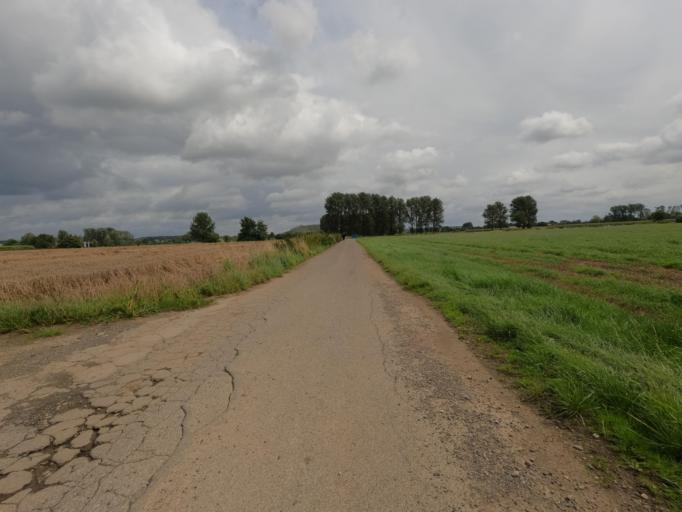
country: DE
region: North Rhine-Westphalia
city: Huckelhoven
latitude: 51.0453
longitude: 6.1849
